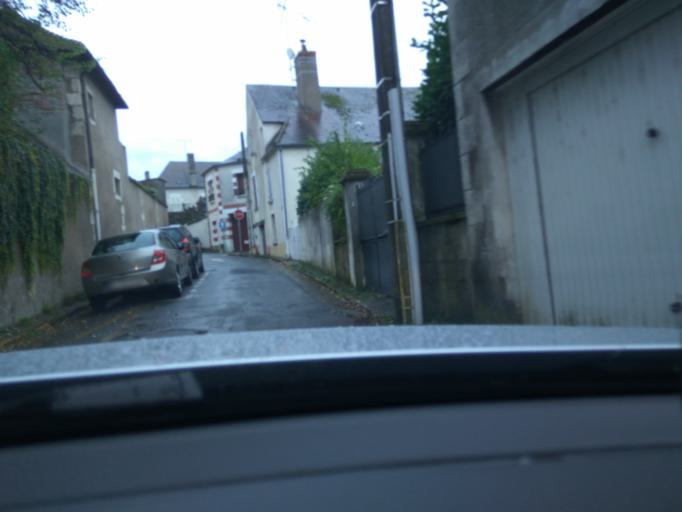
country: FR
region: Centre
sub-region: Departement du Cher
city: Saint-Satur
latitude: 47.3393
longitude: 2.8551
